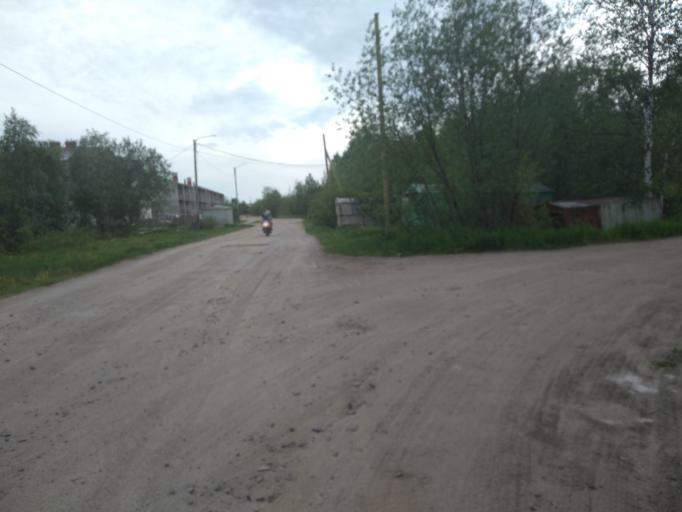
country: RU
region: Komi Republic
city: Pechora
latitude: 65.1419
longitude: 57.2461
